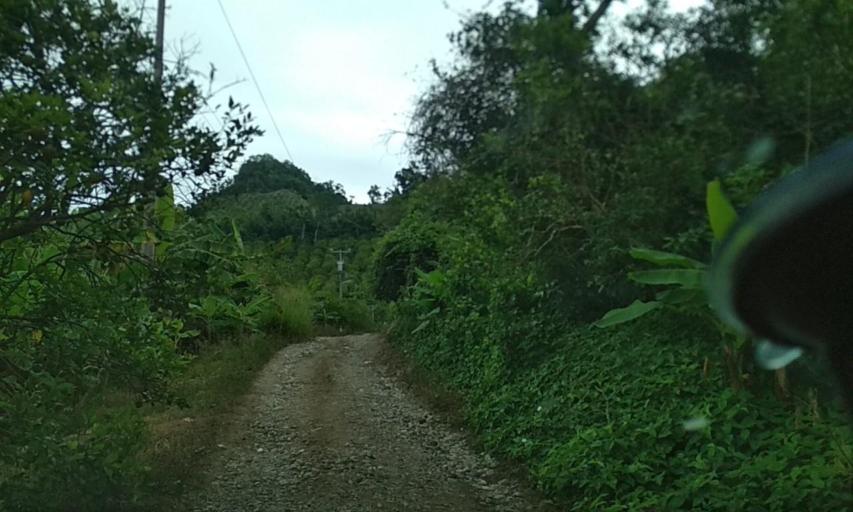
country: MX
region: Veracruz
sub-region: Papantla
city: Residencial Tajin
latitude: 20.6162
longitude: -97.3517
